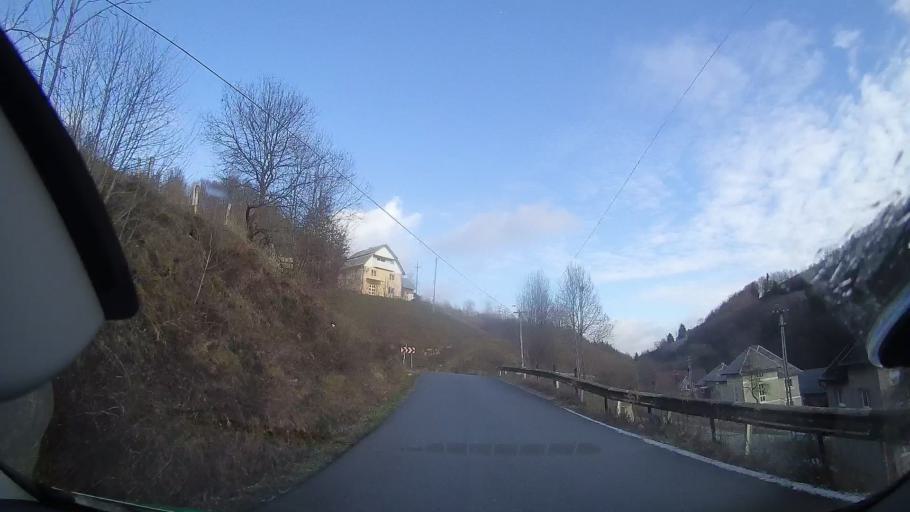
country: RO
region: Alba
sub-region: Comuna Sohodol
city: Sohodol
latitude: 46.3430
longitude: 23.0155
